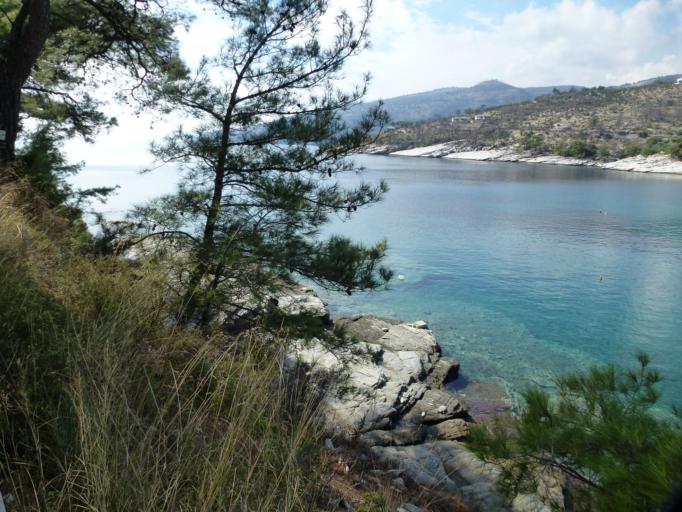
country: GR
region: East Macedonia and Thrace
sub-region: Nomos Kavalas
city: Potamia
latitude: 40.6035
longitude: 24.7407
